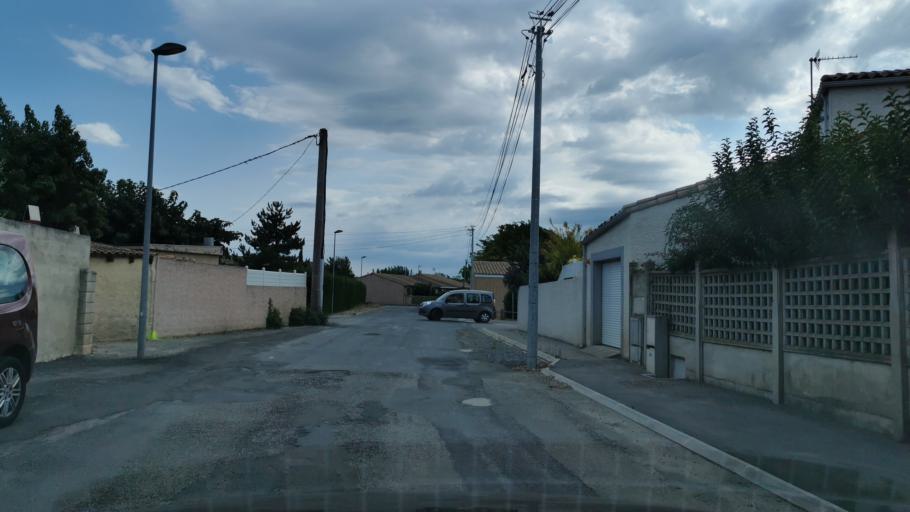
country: FR
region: Languedoc-Roussillon
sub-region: Departement de l'Aude
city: Saint-Marcel-sur-Aude
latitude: 43.2495
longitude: 2.9217
